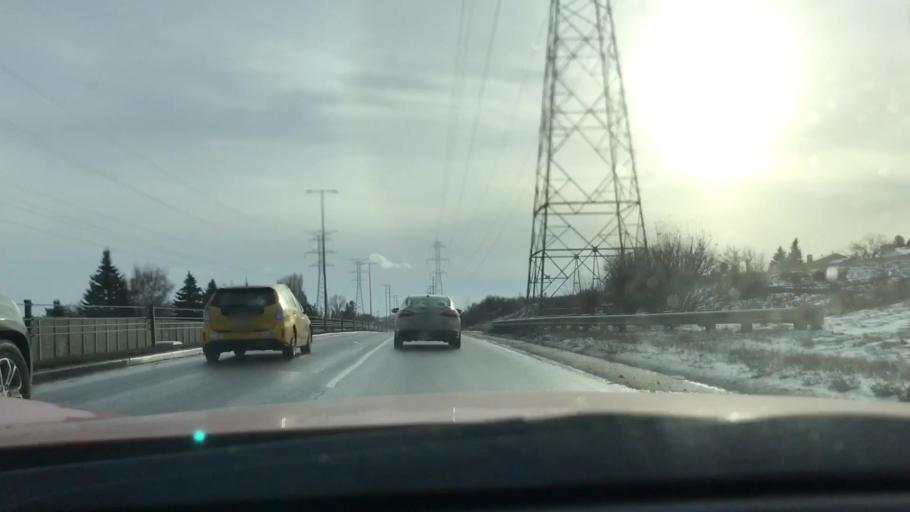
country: CA
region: Alberta
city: Calgary
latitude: 51.0481
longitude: -114.1644
